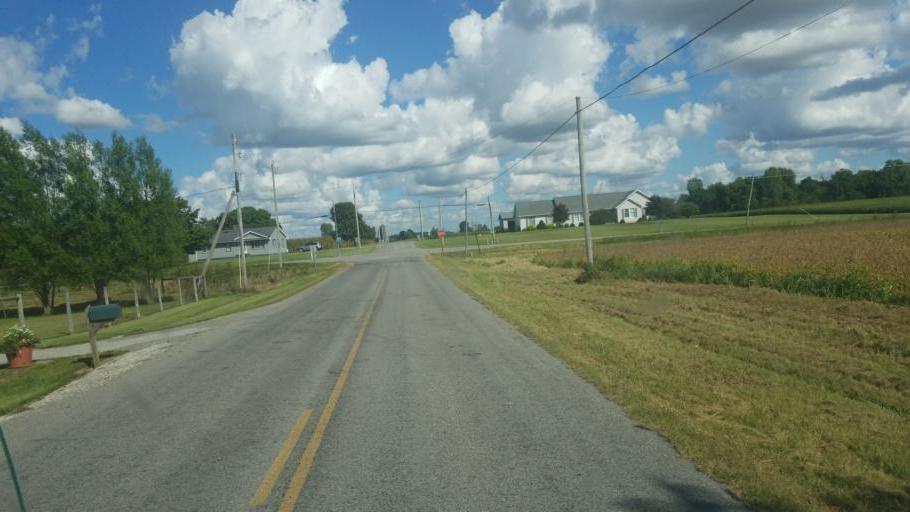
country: US
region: Ohio
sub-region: Hardin County
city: Kenton
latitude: 40.5061
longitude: -83.5749
